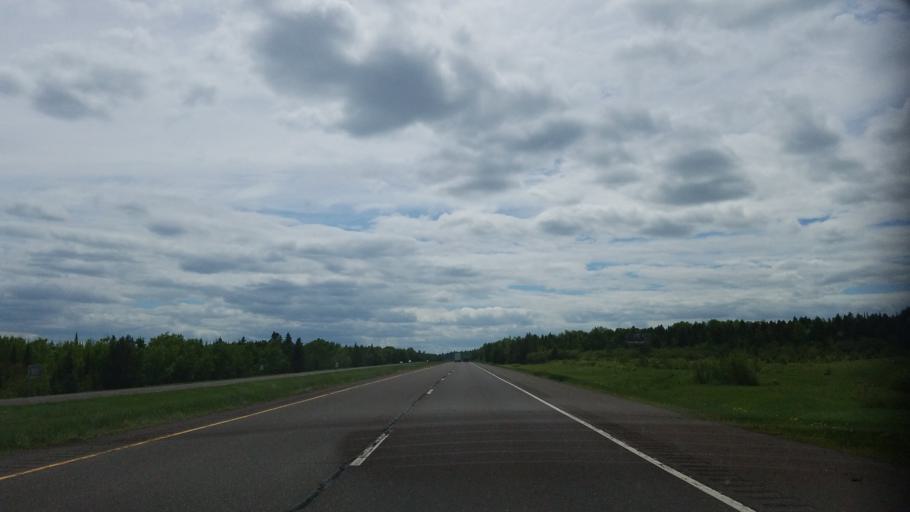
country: US
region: Minnesota
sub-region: Lake County
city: Two Harbors
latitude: 47.0095
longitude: -91.7124
